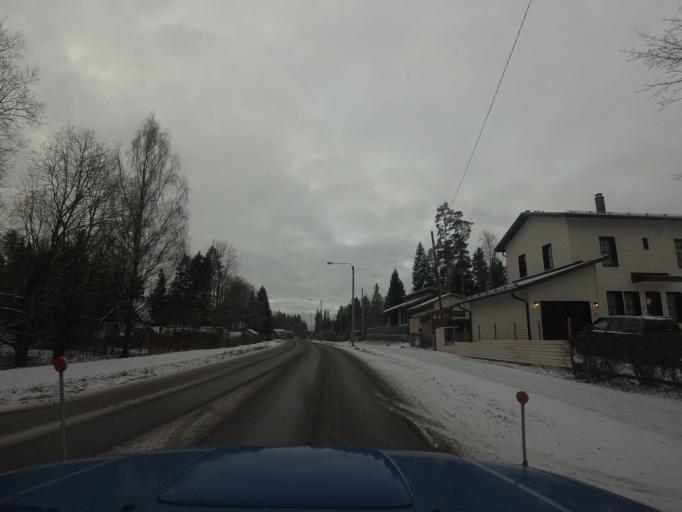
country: FI
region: Uusimaa
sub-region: Helsinki
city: Kilo
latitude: 60.2507
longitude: 24.7763
